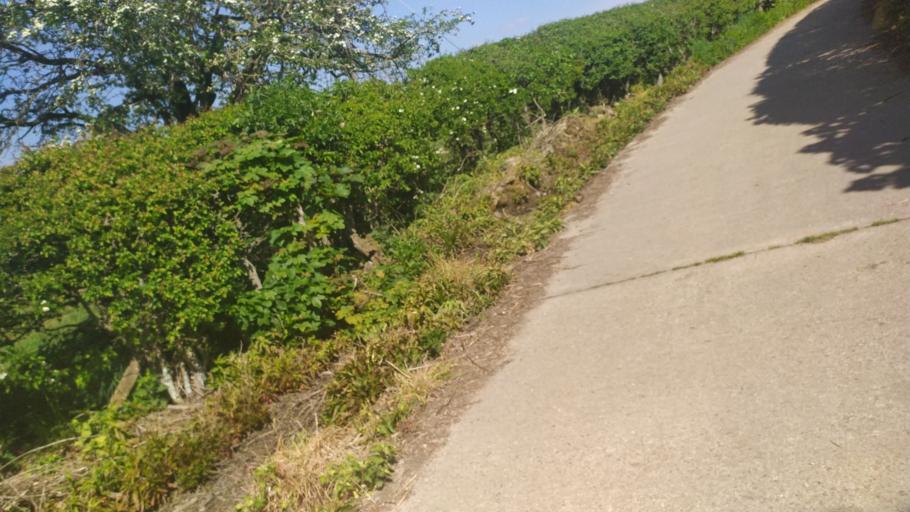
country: GB
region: England
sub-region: City and Borough of Leeds
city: Chapel Allerton
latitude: 53.8773
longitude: -1.5591
